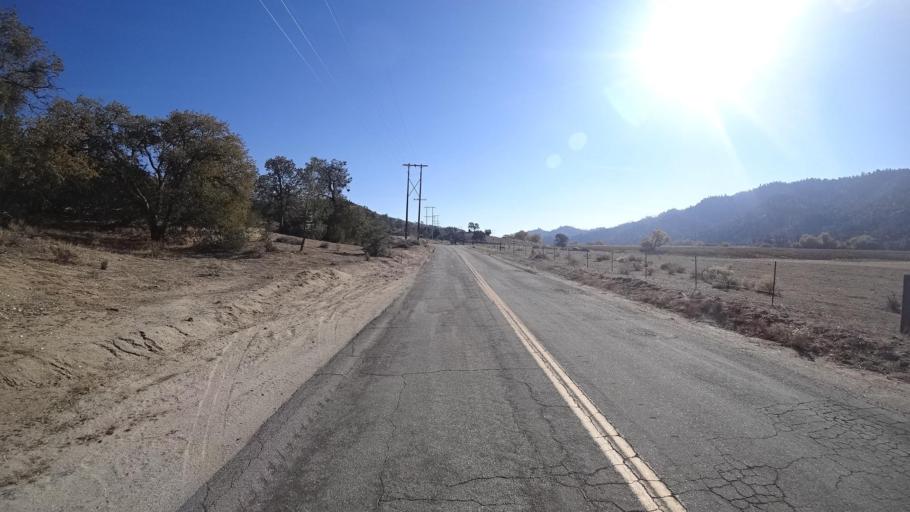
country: US
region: California
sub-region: Kern County
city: Bodfish
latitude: 35.3960
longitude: -118.4410
